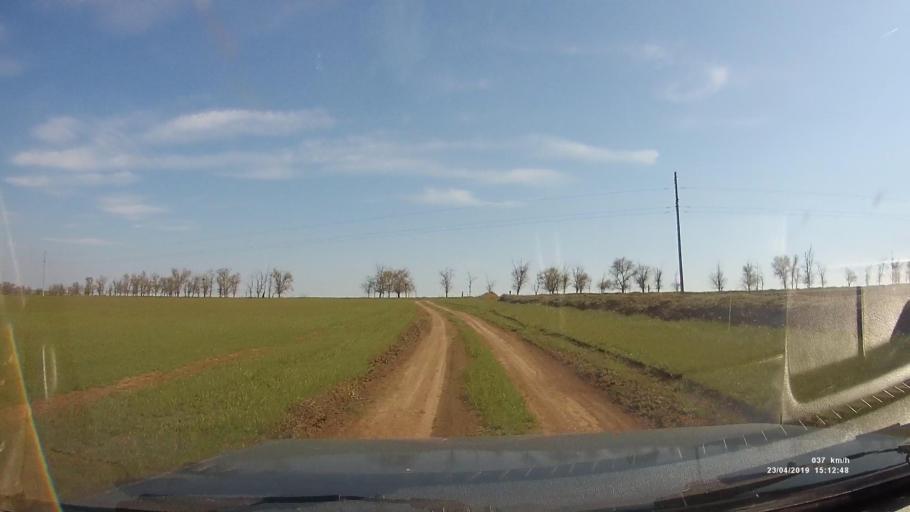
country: RU
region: Rostov
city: Remontnoye
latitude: 46.5416
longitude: 42.9515
